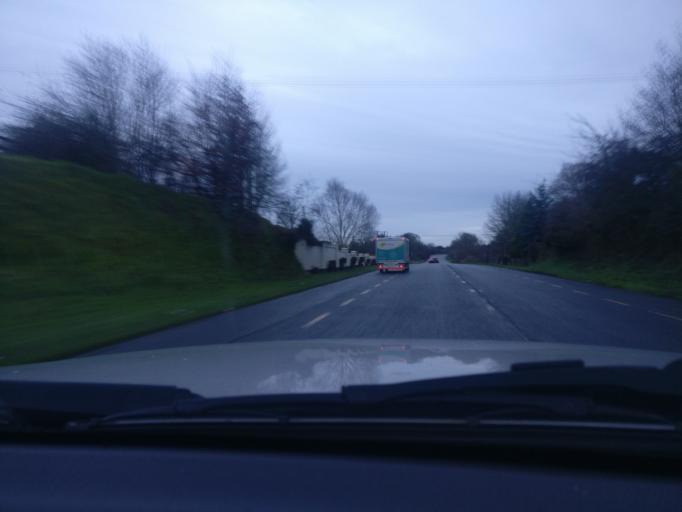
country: IE
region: Leinster
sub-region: An Mhi
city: Kells
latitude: 53.7028
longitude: -6.7941
